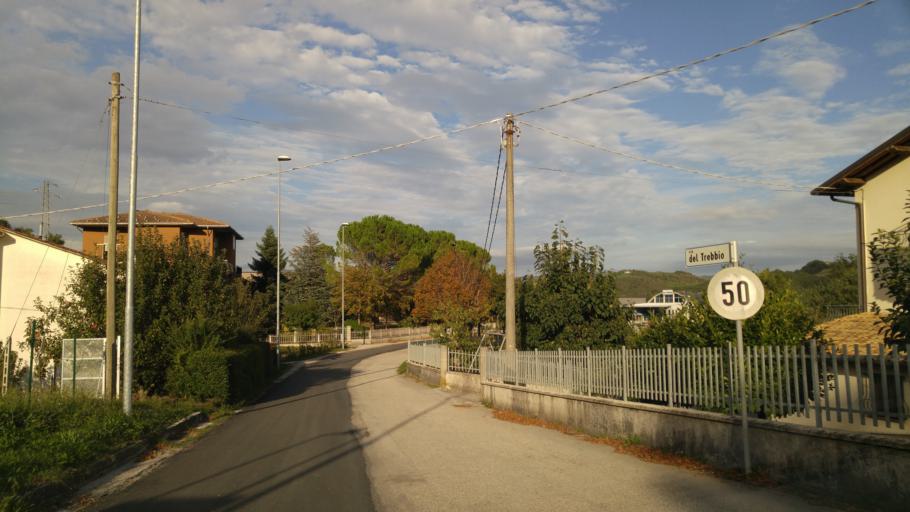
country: IT
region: The Marches
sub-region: Provincia di Pesaro e Urbino
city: Cagli
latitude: 43.5539
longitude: 12.6452
